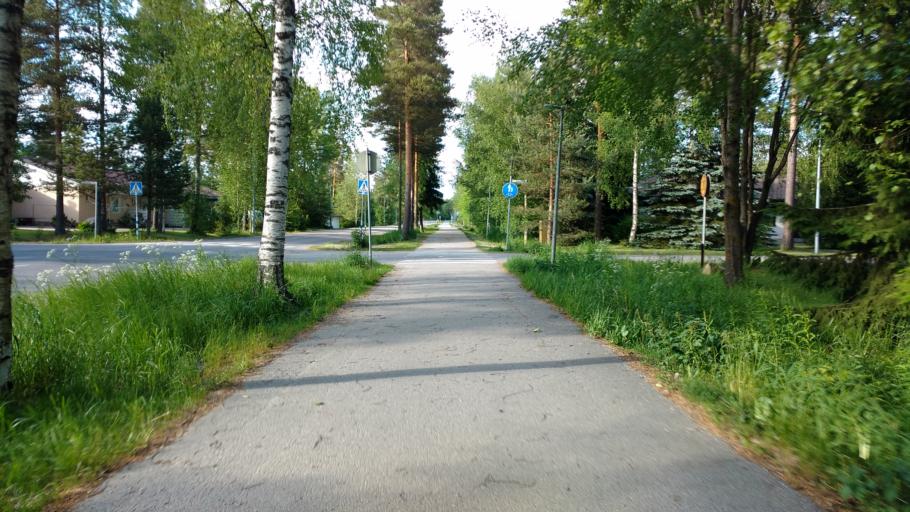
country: FI
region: Varsinais-Suomi
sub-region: Salo
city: Salo
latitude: 60.3910
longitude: 23.1850
